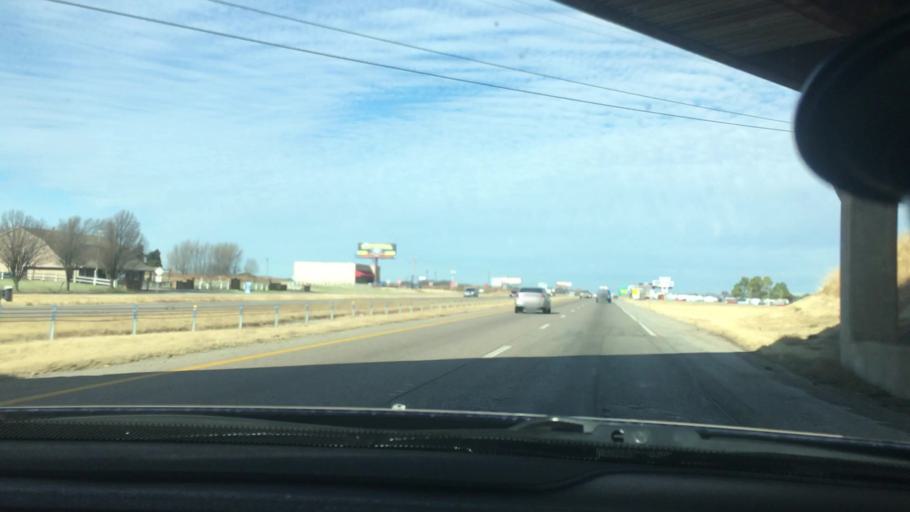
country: US
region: Oklahoma
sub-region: McClain County
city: Goldsby
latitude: 35.1533
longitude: -97.4768
